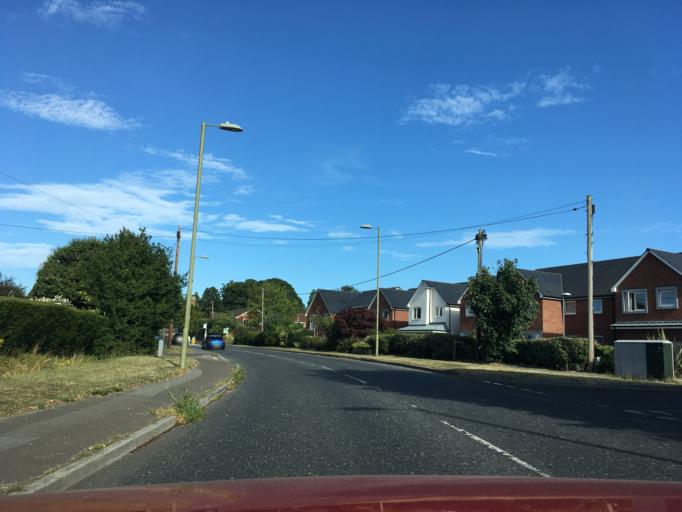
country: GB
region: England
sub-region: Hampshire
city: Romsey
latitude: 50.9887
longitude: -1.4850
